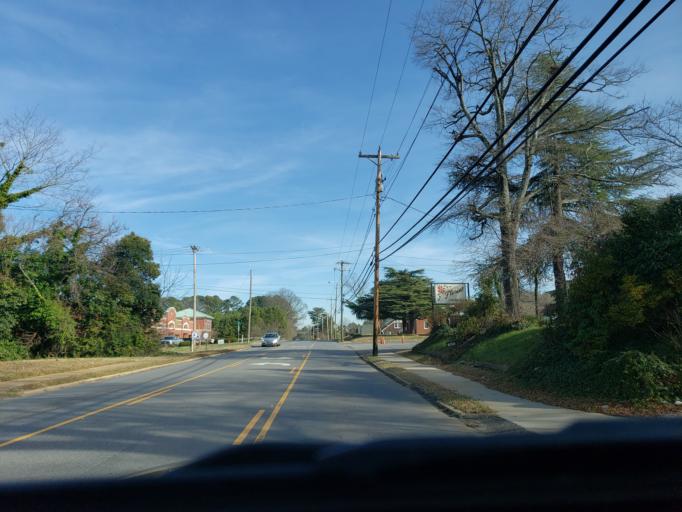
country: US
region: North Carolina
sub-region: Cleveland County
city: Kings Mountain
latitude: 35.2408
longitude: -81.3311
